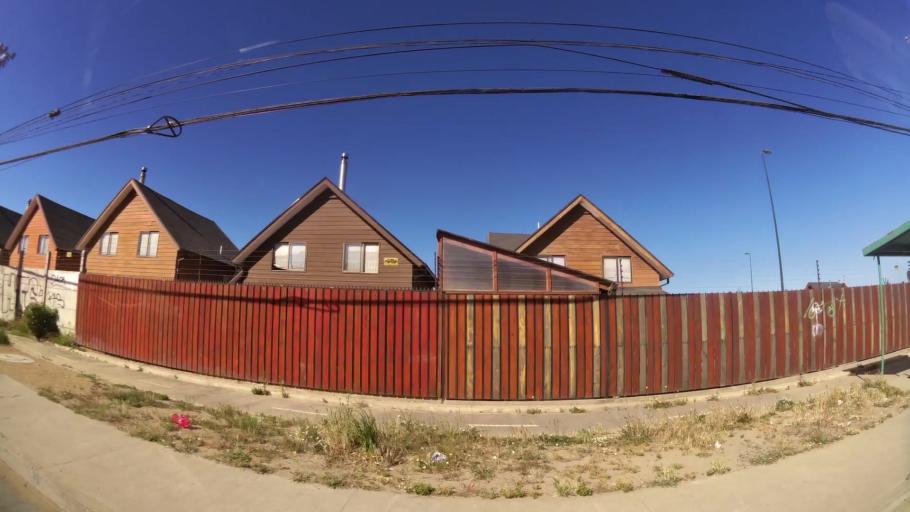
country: CL
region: Valparaiso
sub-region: Provincia de Valparaiso
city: Vina del Mar
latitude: -33.1288
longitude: -71.5684
